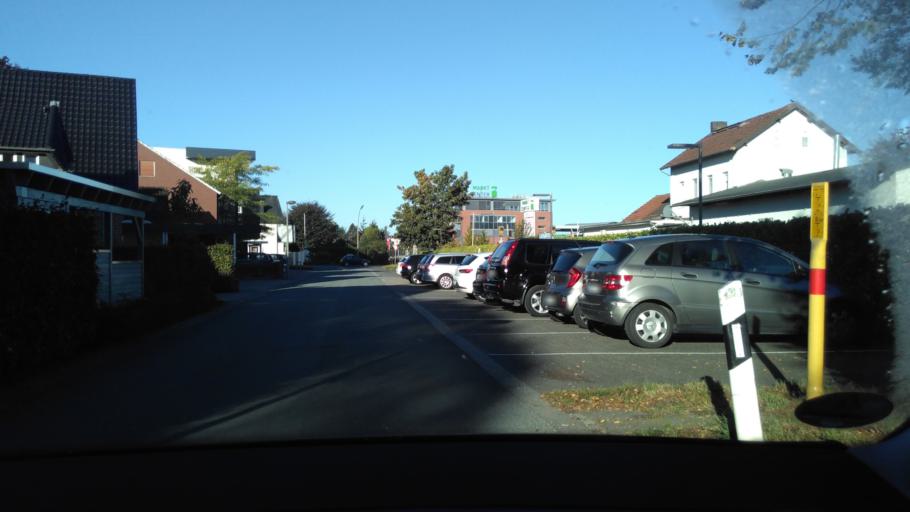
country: DE
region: North Rhine-Westphalia
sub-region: Regierungsbezirk Detmold
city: Verl
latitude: 51.8807
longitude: 8.5102
